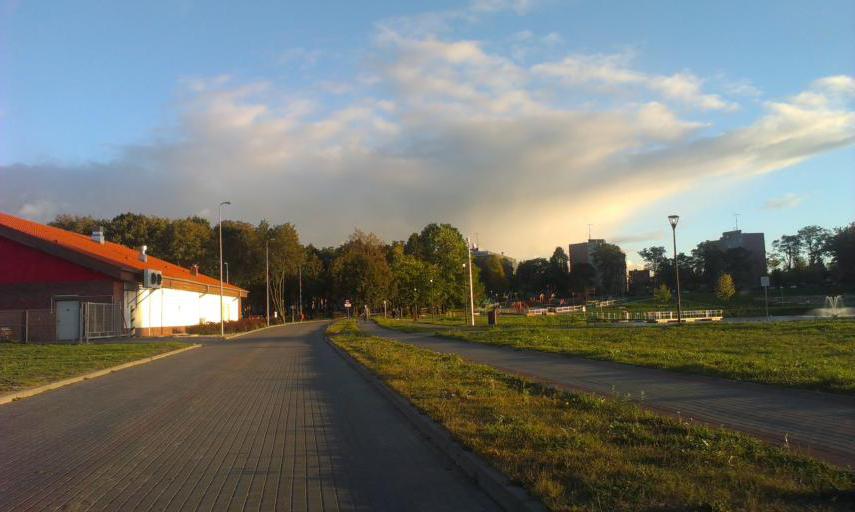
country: PL
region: West Pomeranian Voivodeship
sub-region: Powiat szczecinecki
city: Szczecinek
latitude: 53.7082
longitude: 16.7074
